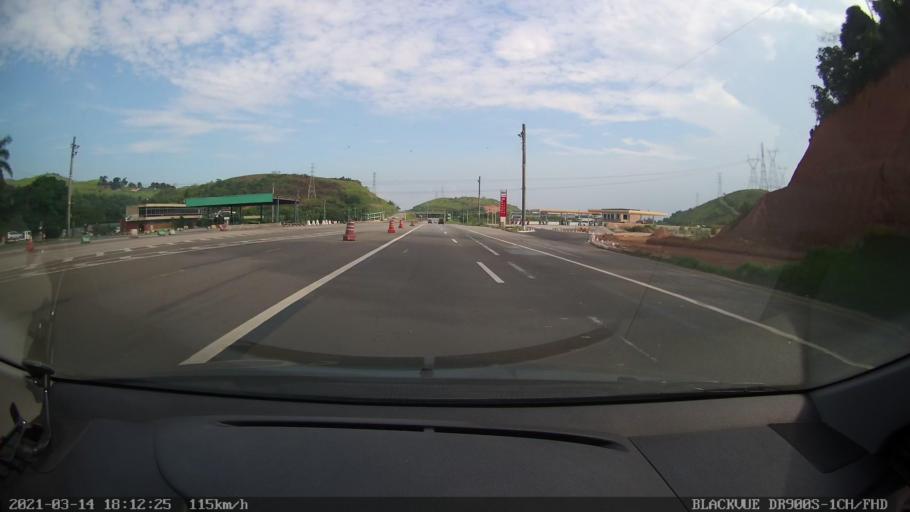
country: BR
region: Rio de Janeiro
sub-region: Duque De Caxias
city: Duque de Caxias
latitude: -22.6295
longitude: -43.2858
